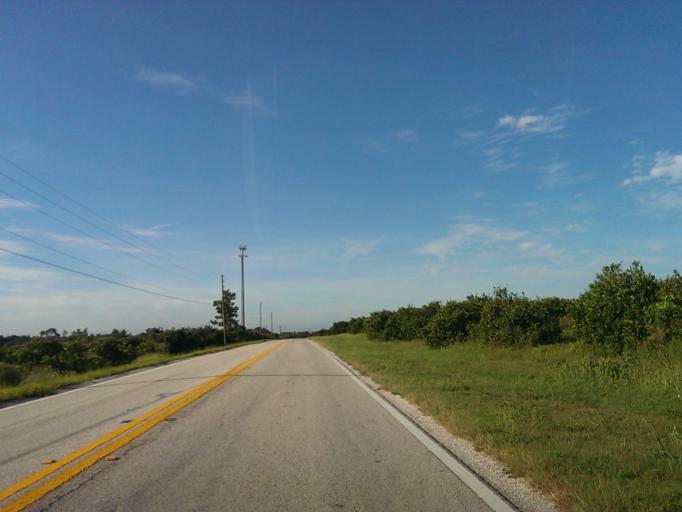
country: US
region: Florida
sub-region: Polk County
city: Citrus Ridge
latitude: 28.3788
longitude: -81.6437
